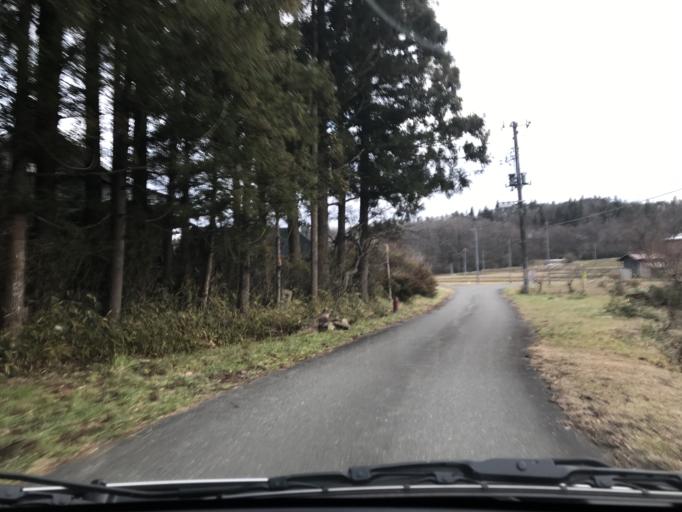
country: JP
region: Iwate
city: Ichinoseki
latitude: 38.9708
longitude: 141.0600
